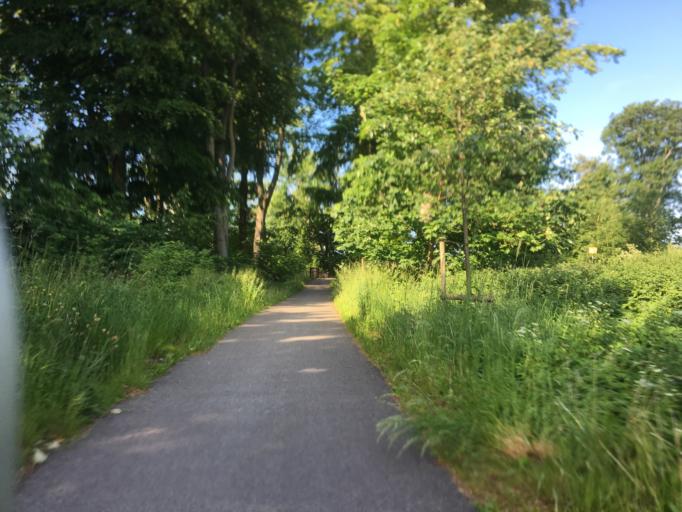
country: SE
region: Skane
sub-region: Ystads Kommun
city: Ystad
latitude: 55.4243
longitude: 13.6992
